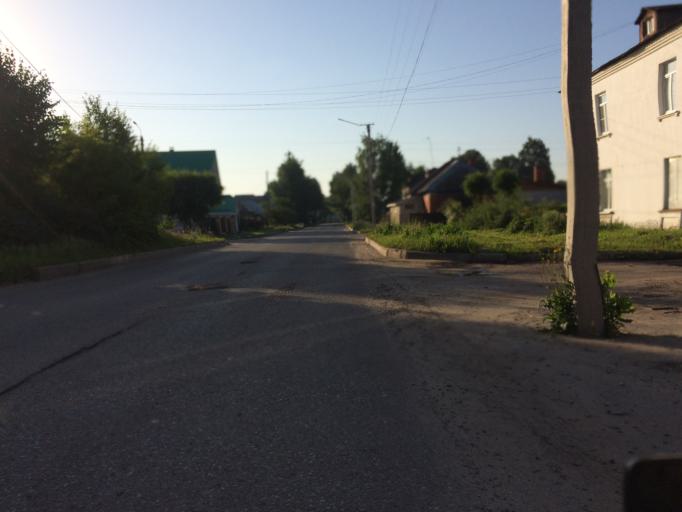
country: RU
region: Mariy-El
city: Yoshkar-Ola
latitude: 56.6517
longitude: 47.9001
